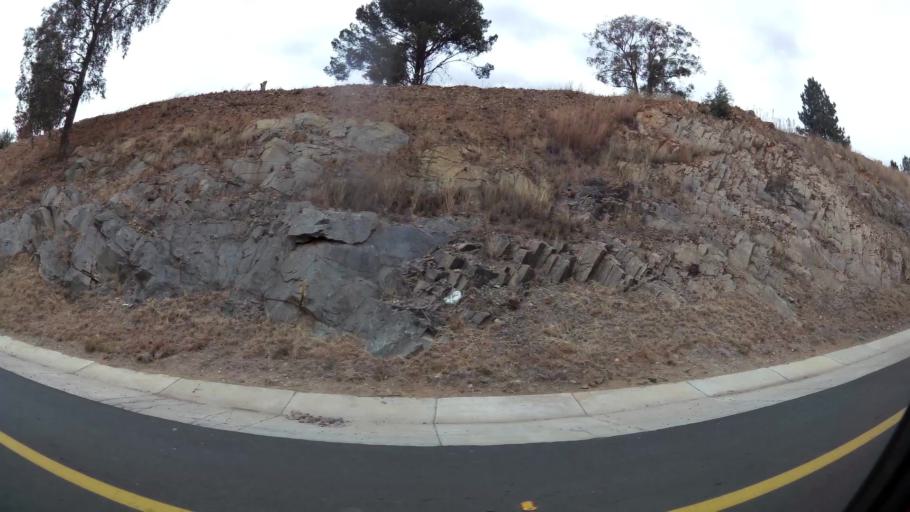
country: ZA
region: Gauteng
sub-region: West Rand District Municipality
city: Muldersdriseloop
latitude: -26.0214
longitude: 27.8577
